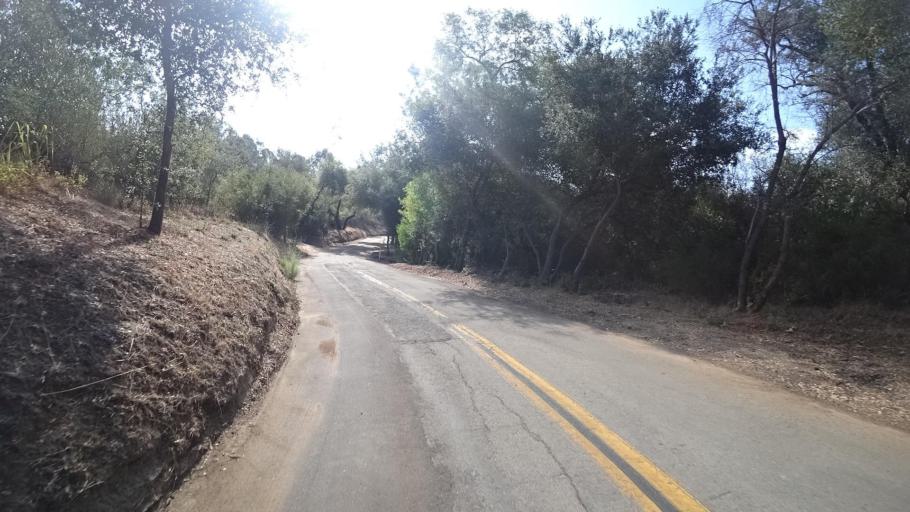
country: US
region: California
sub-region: San Diego County
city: San Marcos
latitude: 33.0896
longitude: -117.1658
